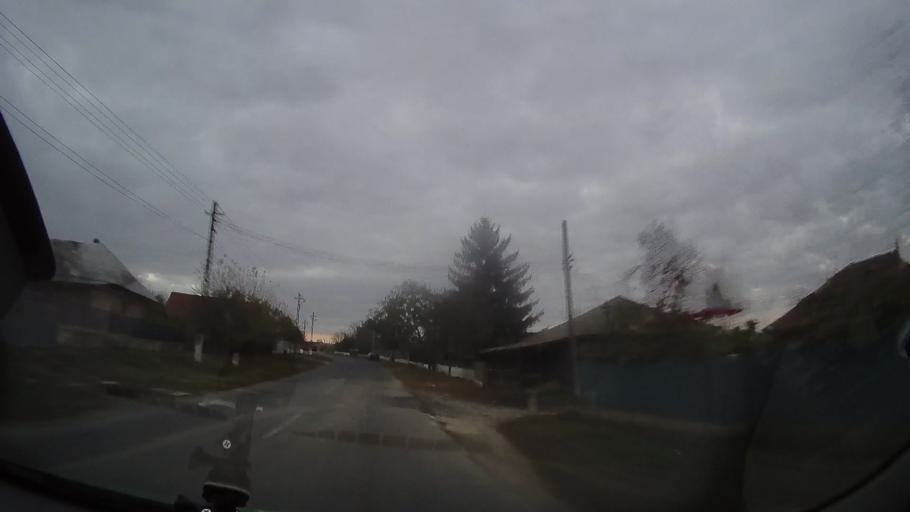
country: RO
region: Tulcea
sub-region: Comuna Mihai Bravu
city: Turda
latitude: 44.9706
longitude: 28.6278
